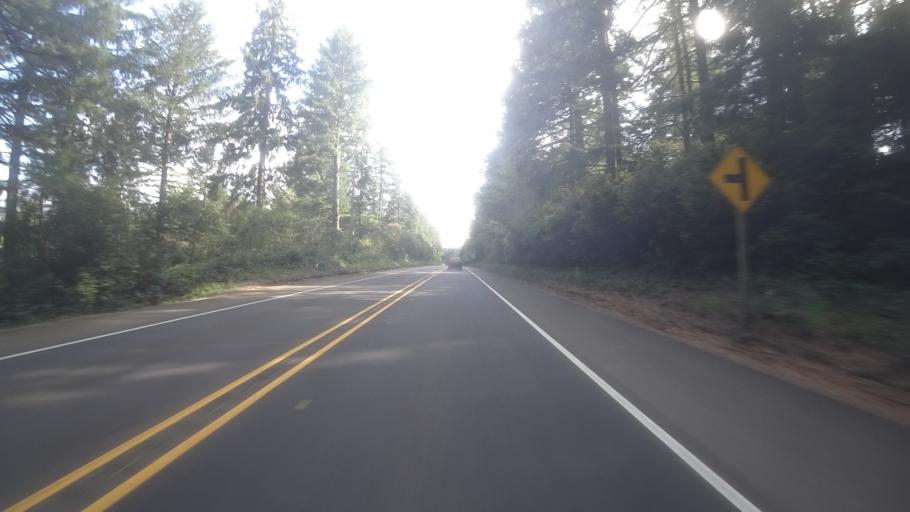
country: US
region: Oregon
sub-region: Lane County
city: Dunes City
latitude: 43.9193
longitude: -124.1089
